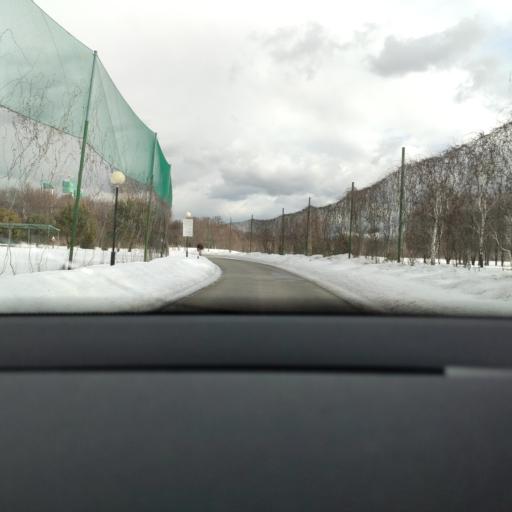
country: RU
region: Moskovskaya
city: Fili
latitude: 55.7592
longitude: 37.4579
